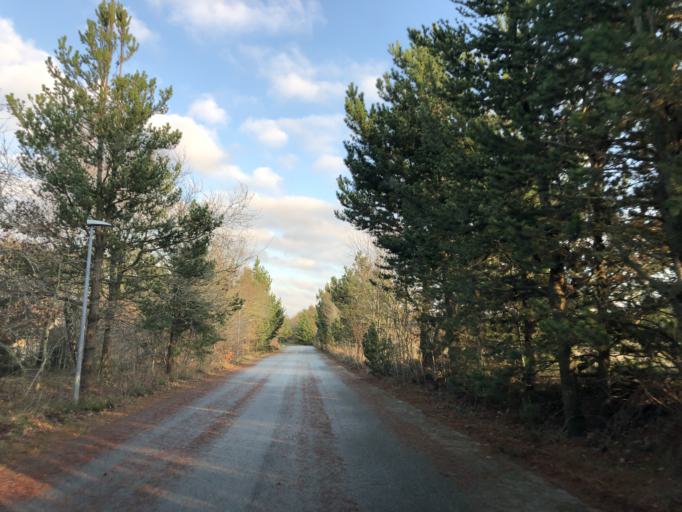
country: DK
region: Central Jutland
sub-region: Holstebro Kommune
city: Ulfborg
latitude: 56.3184
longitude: 8.4352
